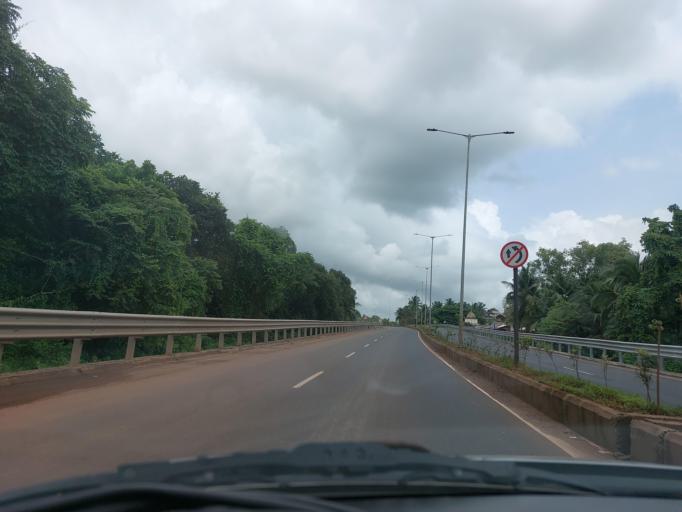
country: IN
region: Goa
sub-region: North Goa
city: Queula
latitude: 15.3839
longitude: 74.0022
